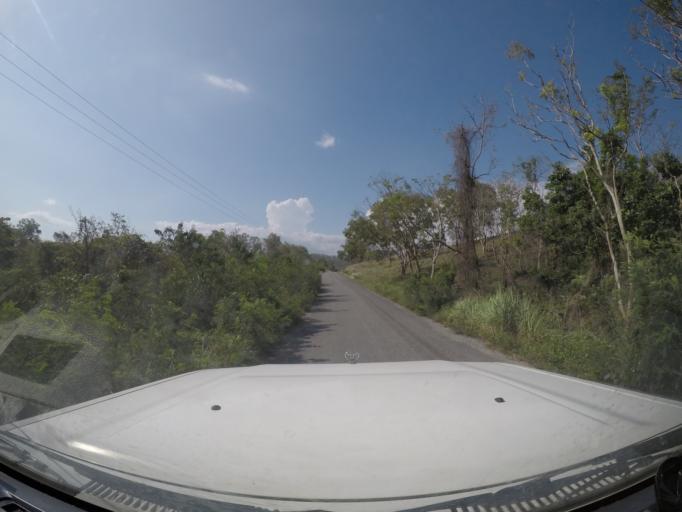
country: PG
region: Central Province
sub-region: Rigo
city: Kwikila
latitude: -9.8647
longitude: 147.5627
